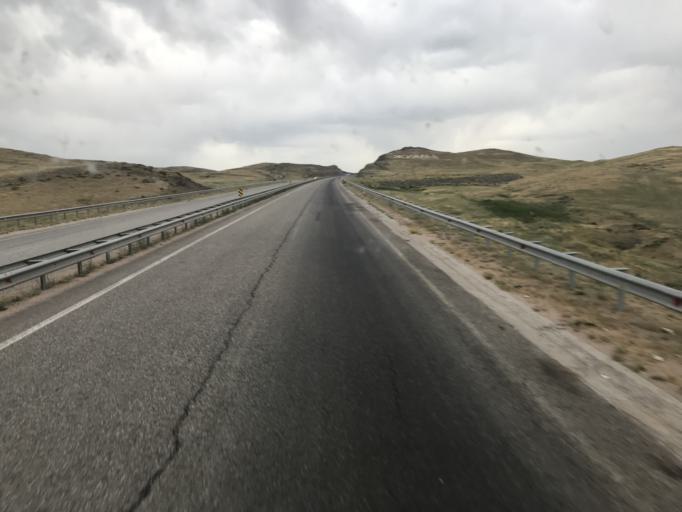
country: KZ
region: Zhambyl
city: Taraz
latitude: 42.7510
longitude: 71.0146
